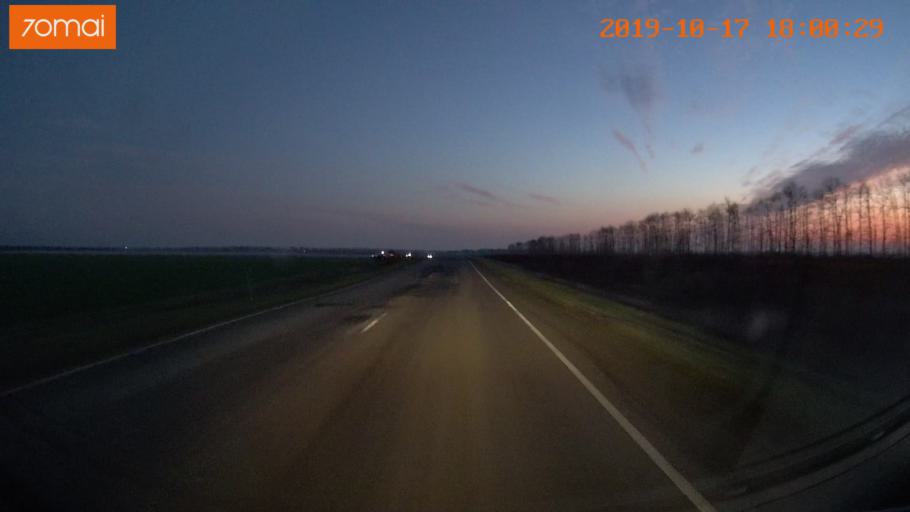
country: RU
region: Tula
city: Kurkino
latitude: 53.5206
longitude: 38.6152
